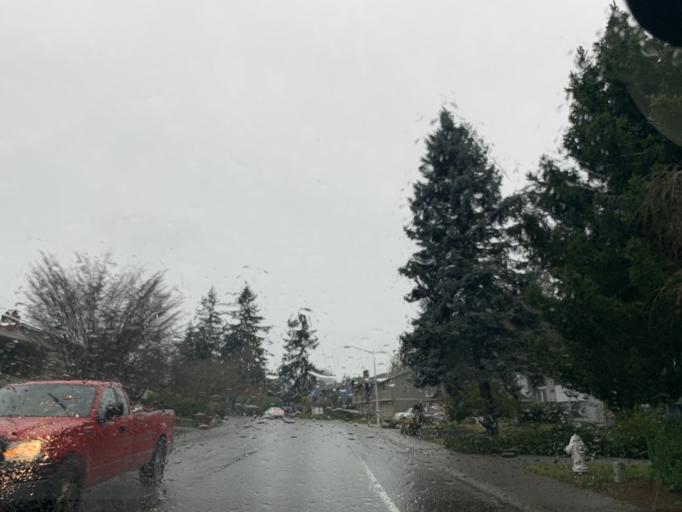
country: US
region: Washington
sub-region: King County
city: Kingsgate
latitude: 47.7420
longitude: -122.1812
